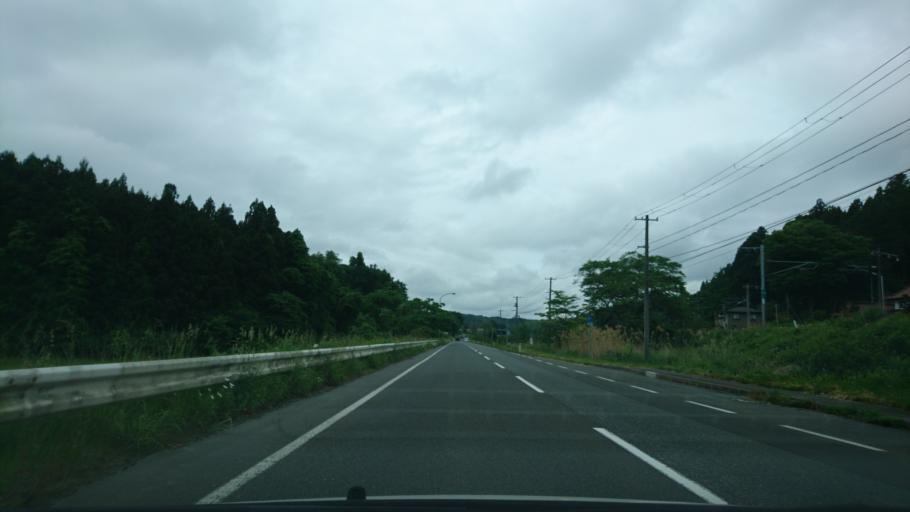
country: JP
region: Iwate
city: Ichinoseki
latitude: 38.8971
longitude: 141.1272
